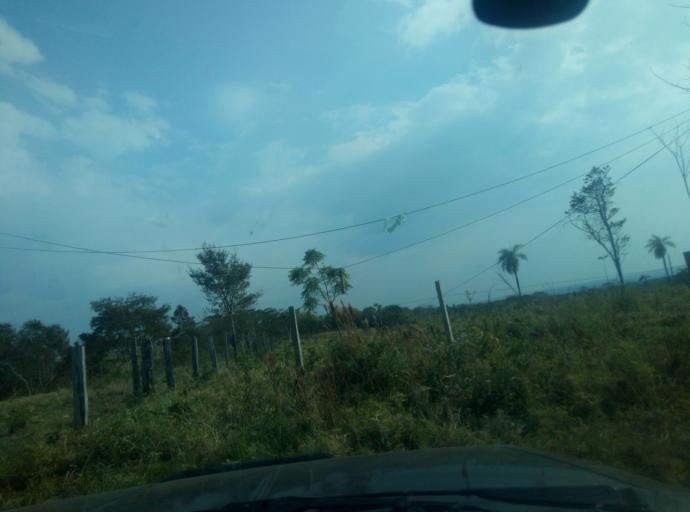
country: PY
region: Caaguazu
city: Doctor Cecilio Baez
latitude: -25.1809
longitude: -56.1354
